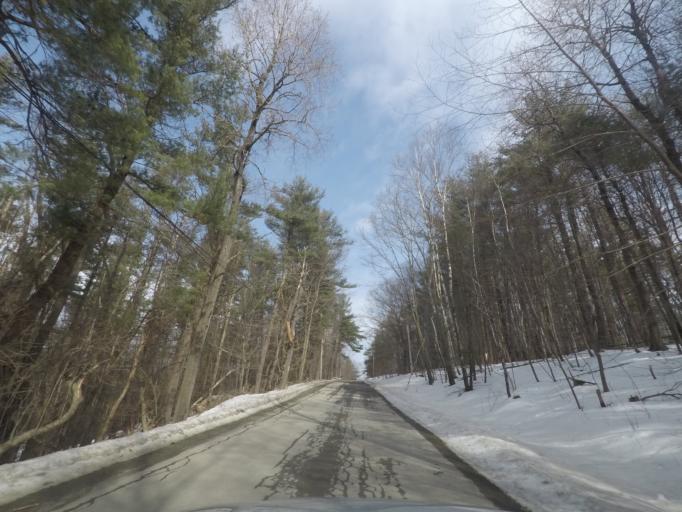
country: US
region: New York
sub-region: Saratoga County
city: Waterford
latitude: 42.7765
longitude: -73.6020
